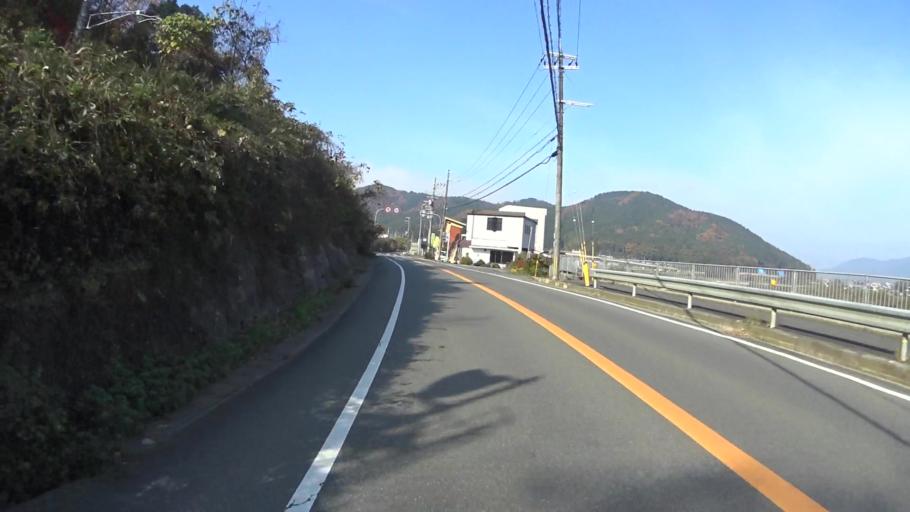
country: JP
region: Kyoto
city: Fukuchiyama
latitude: 35.2740
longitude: 135.1418
